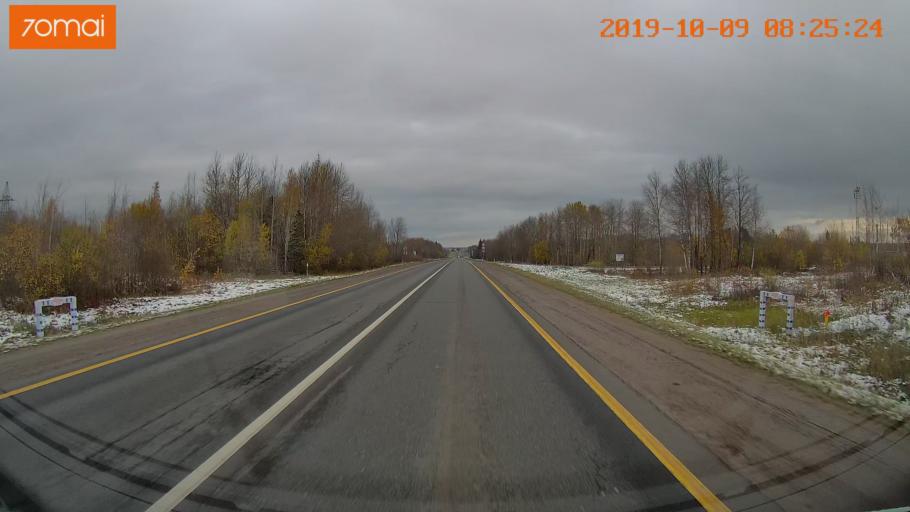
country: RU
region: Vologda
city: Gryazovets
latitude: 58.7805
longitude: 40.2725
